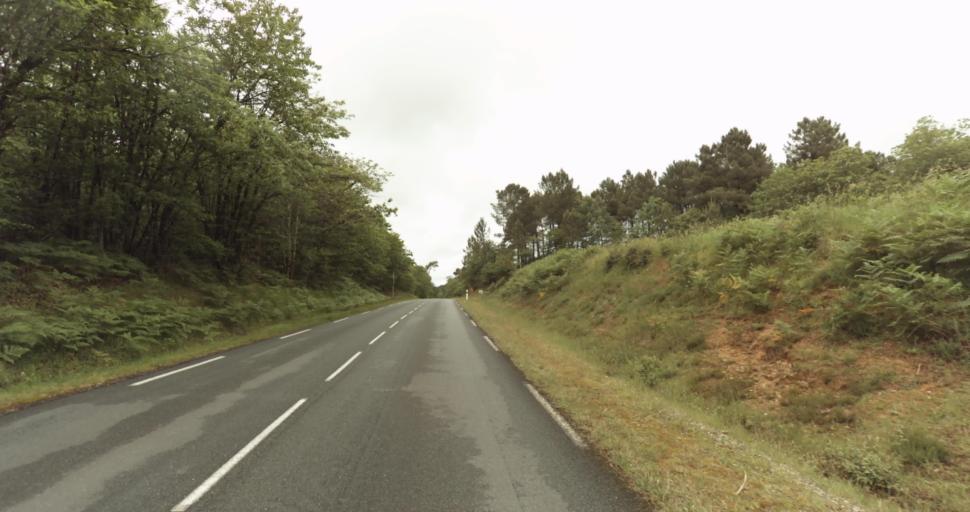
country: FR
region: Aquitaine
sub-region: Departement de la Dordogne
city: Belves
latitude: 44.6707
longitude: 1.0002
